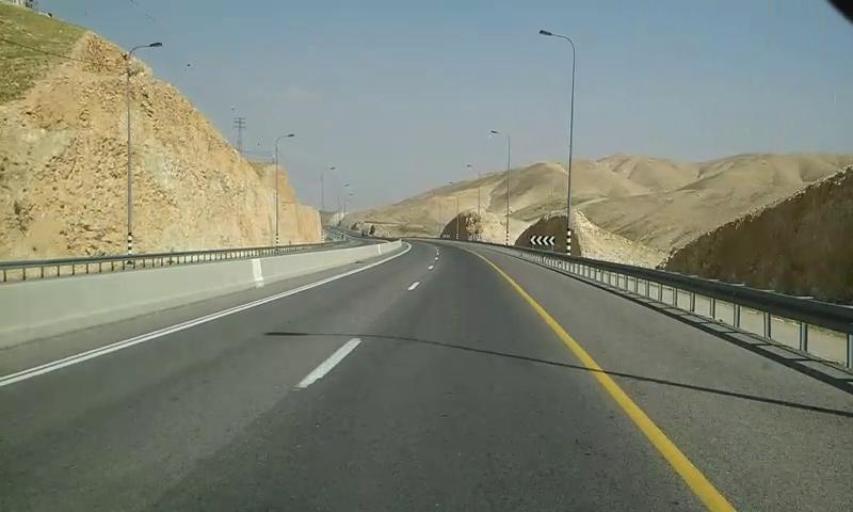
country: PS
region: West Bank
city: Jericho
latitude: 31.8159
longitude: 35.3703
